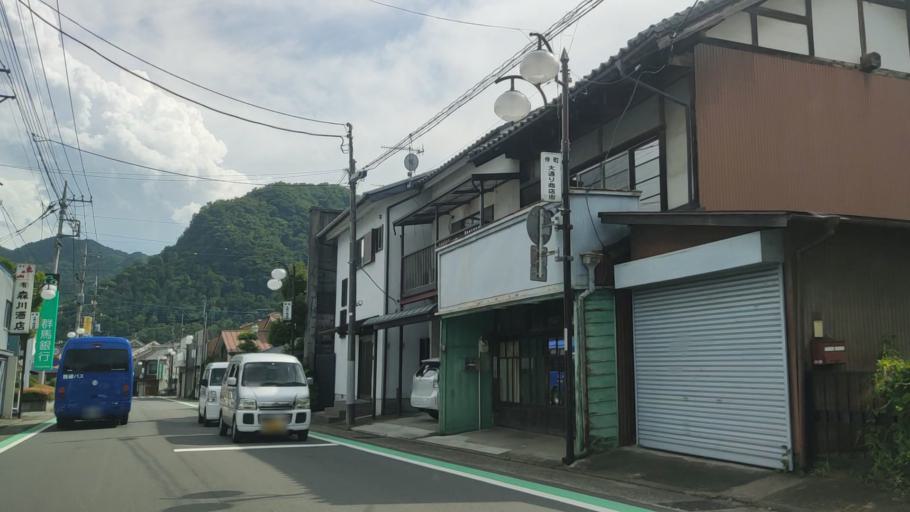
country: JP
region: Gunma
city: Tomioka
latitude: 36.2116
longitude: 138.7826
